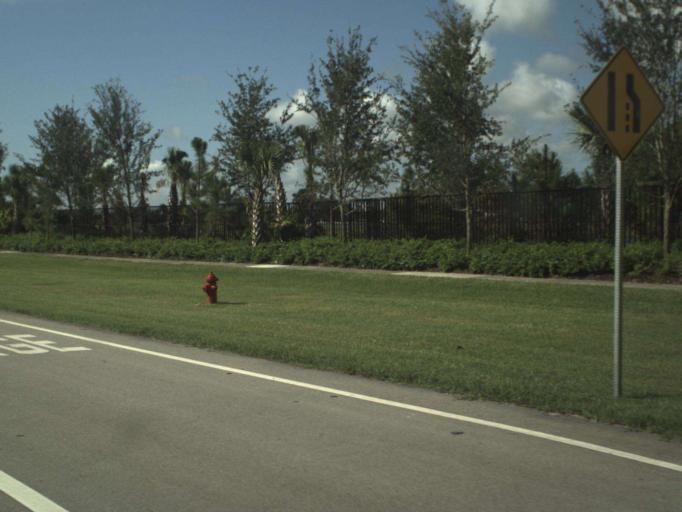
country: US
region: Florida
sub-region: Indian River County
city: Gifford
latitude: 27.6831
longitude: -80.4048
